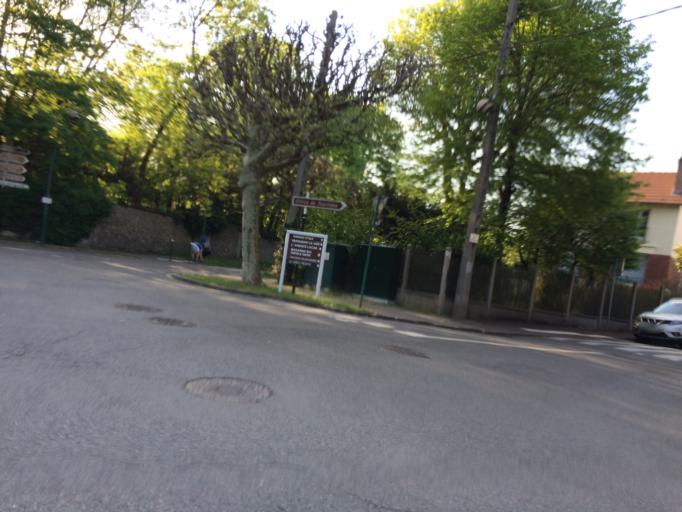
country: FR
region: Ile-de-France
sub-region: Departement de l'Essonne
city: Verrieres-le-Buisson
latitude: 48.7442
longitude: 2.2668
